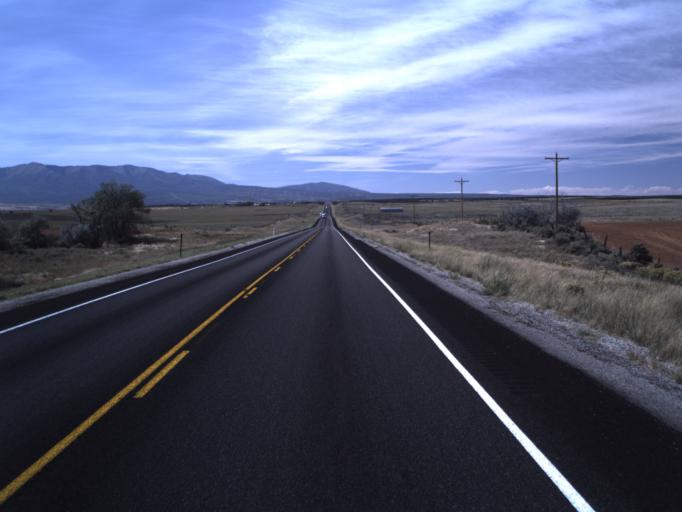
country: US
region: Utah
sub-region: San Juan County
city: Monticello
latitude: 37.8473
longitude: -109.1522
